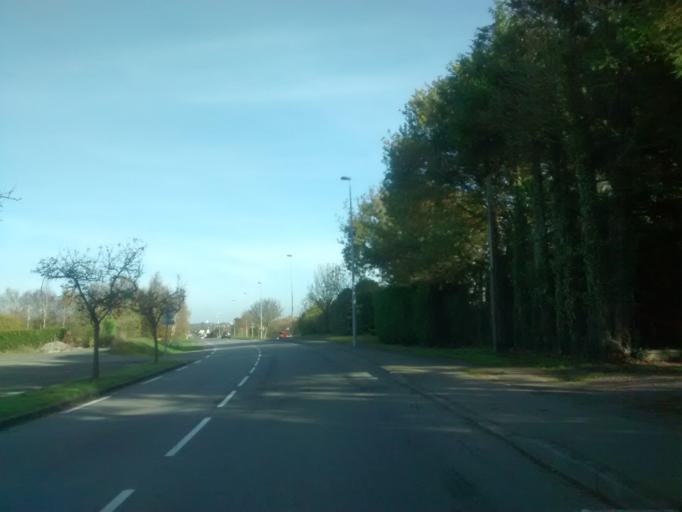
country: FR
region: Brittany
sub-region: Departement d'Ille-et-Vilaine
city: Chantepie
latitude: 48.1027
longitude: -1.6042
